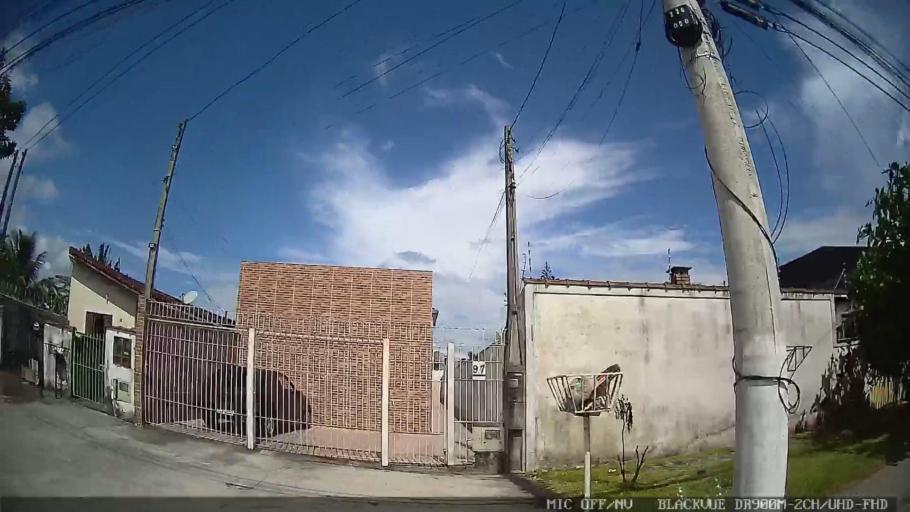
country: BR
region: Sao Paulo
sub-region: Caraguatatuba
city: Caraguatatuba
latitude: -23.6330
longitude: -45.4394
